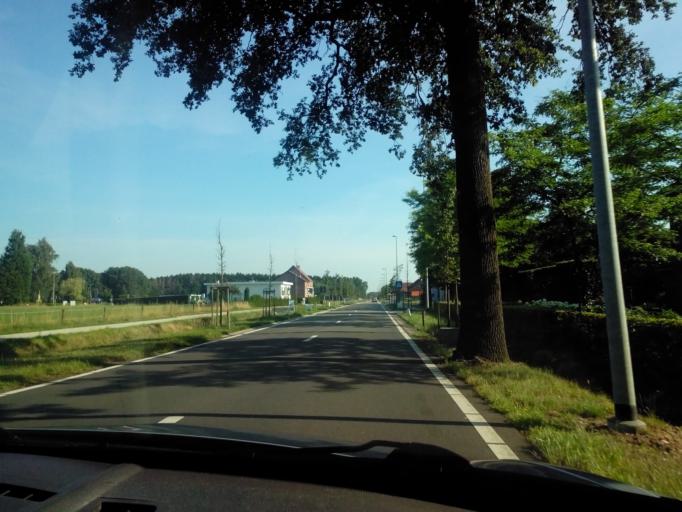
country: BE
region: Flanders
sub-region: Provincie Limburg
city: Opglabbeek
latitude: 51.0740
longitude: 5.5860
